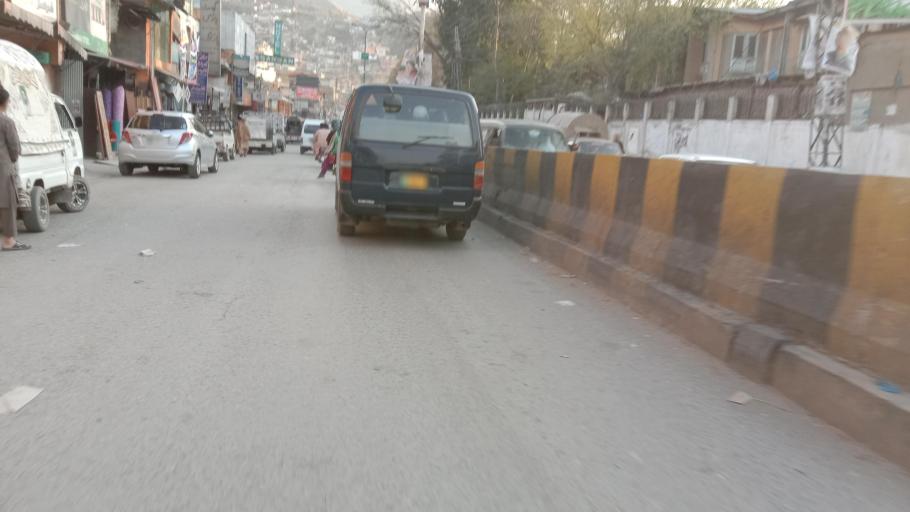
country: PK
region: Khyber Pakhtunkhwa
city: Abbottabad
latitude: 34.1461
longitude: 73.2154
